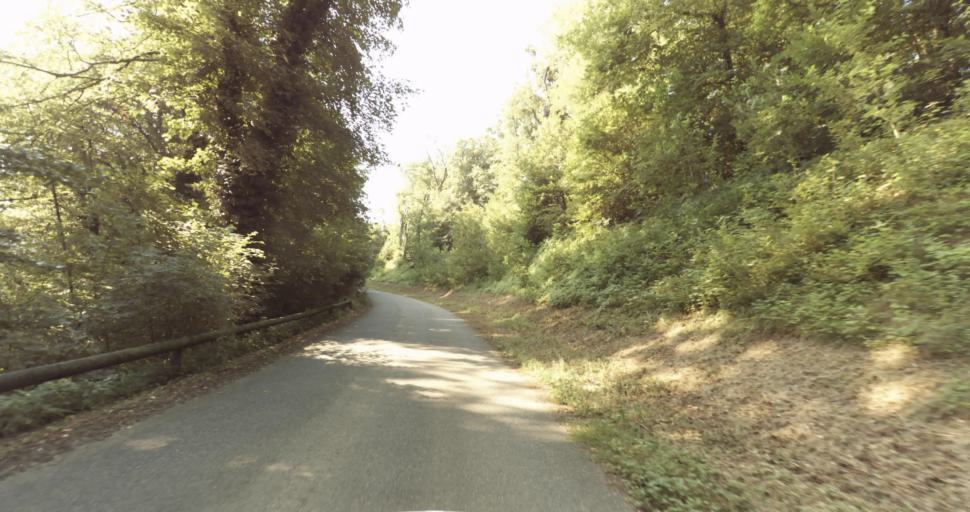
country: FR
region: Lorraine
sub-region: Departement de Meurthe-et-Moselle
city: Briey
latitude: 49.2499
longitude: 5.9284
